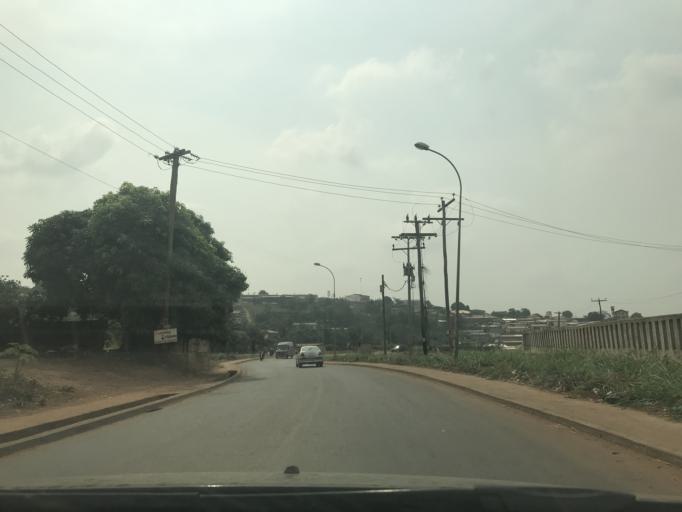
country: CM
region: Centre
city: Yaounde
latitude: 3.8327
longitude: 11.5154
